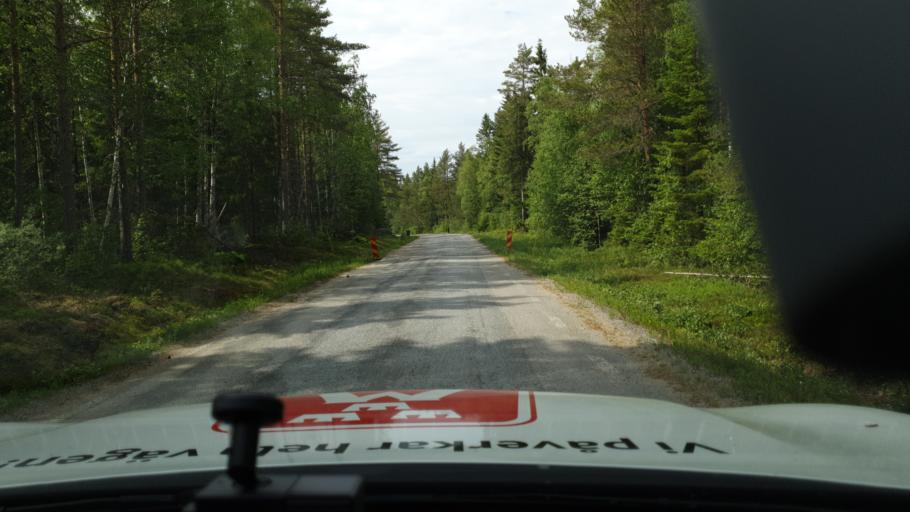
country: SE
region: Vaesterbotten
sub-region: Umea Kommun
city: Hoernefors
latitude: 63.5024
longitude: 19.7349
